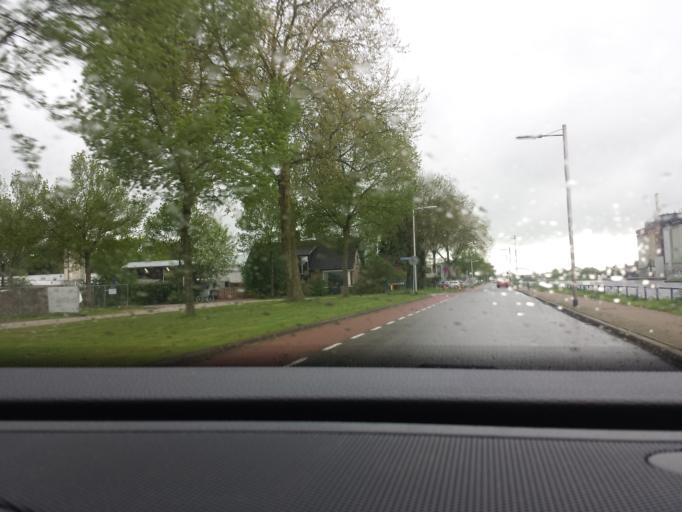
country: NL
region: Gelderland
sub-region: Gemeente Lochem
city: Lochem
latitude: 52.1657
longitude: 6.4097
